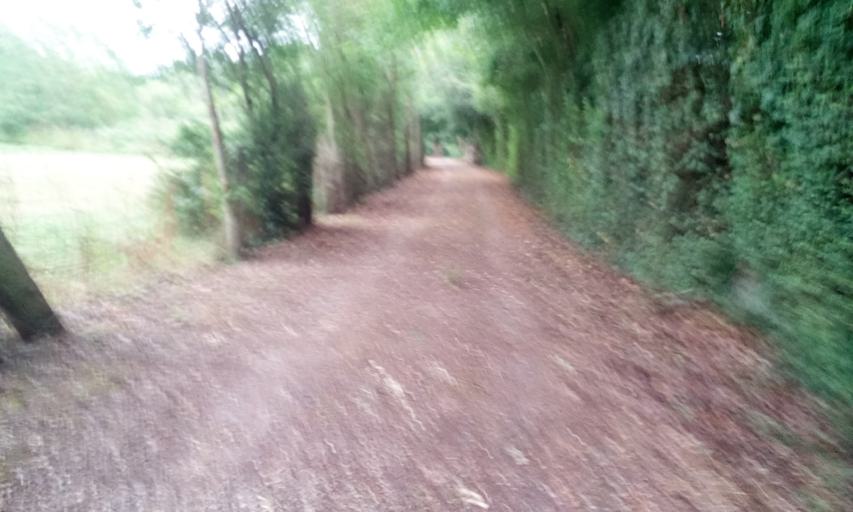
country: FR
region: Lower Normandy
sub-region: Departement du Calvados
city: Sannerville
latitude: 49.1988
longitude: -0.2214
